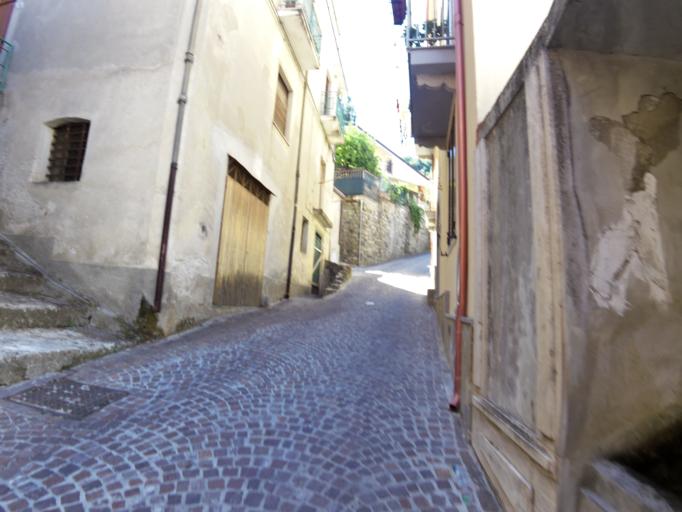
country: IT
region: Calabria
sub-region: Provincia di Reggio Calabria
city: Bivongi
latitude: 38.4820
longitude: 16.4522
